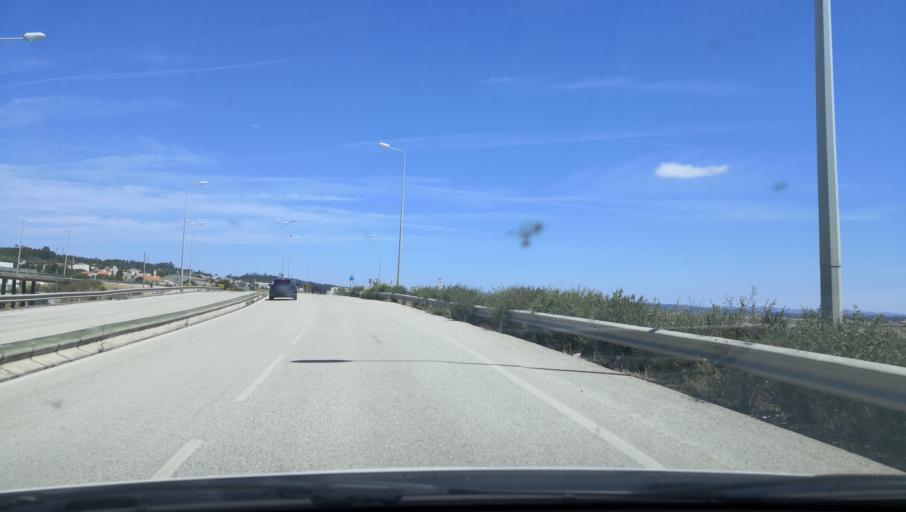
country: PT
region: Coimbra
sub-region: Figueira da Foz
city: Tavarede
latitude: 40.1473
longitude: -8.8344
